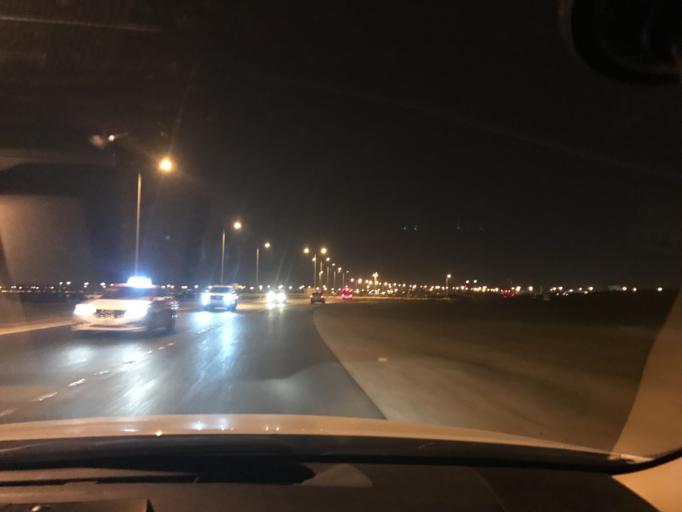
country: BH
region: Muharraq
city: Al Hadd
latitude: 26.2620
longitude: 50.6553
